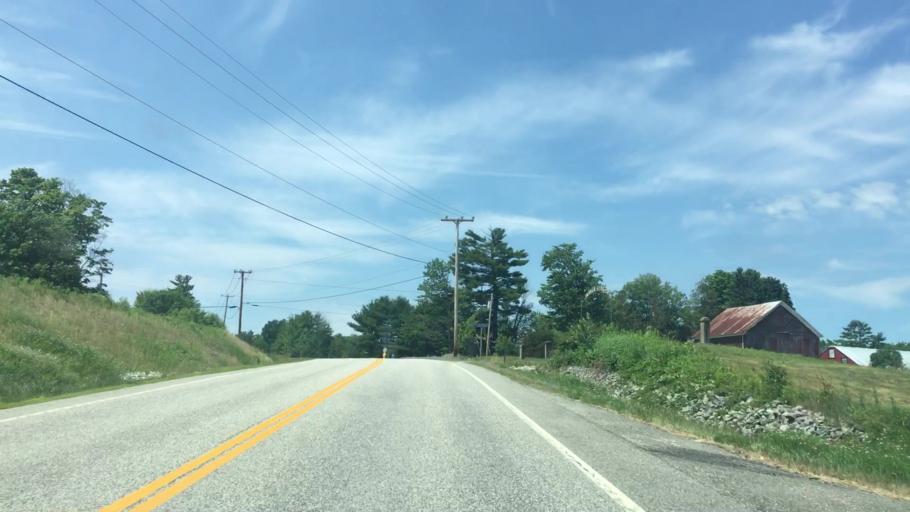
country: US
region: Maine
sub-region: Androscoggin County
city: Leeds
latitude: 44.3458
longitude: -70.1529
